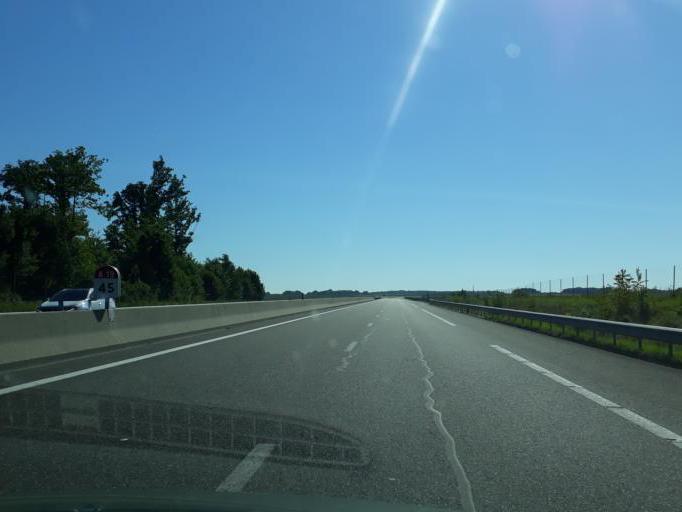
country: FR
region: Centre
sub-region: Departement du Loiret
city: Saint-Germain-des-Pres
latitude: 48.0444
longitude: 2.9046
